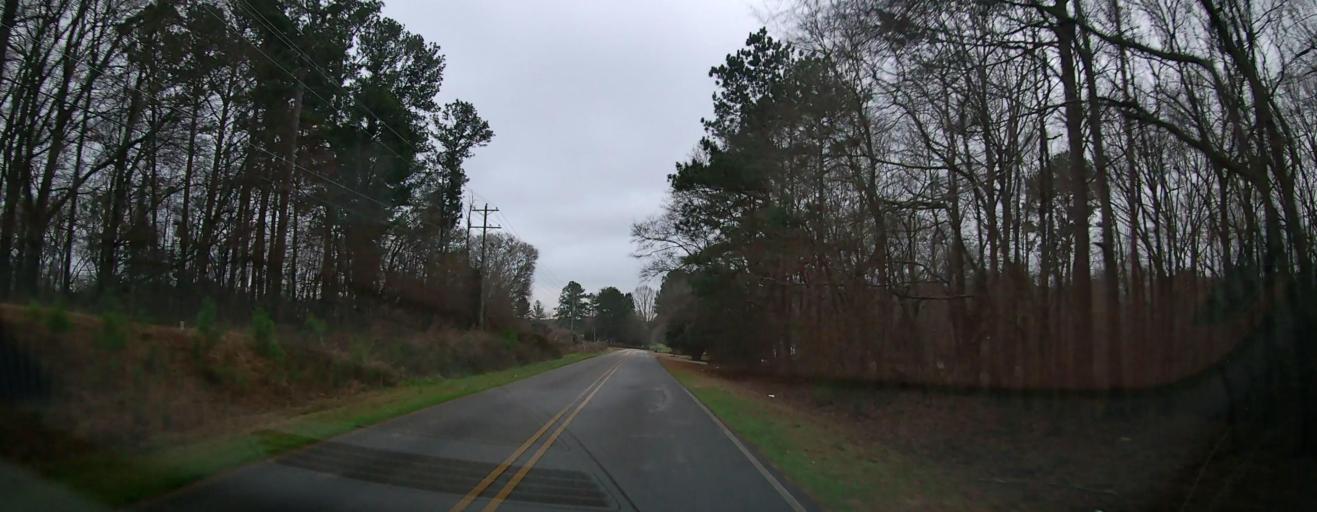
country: US
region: Georgia
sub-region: Lamar County
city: Barnesville
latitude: 33.0495
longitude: -84.1096
